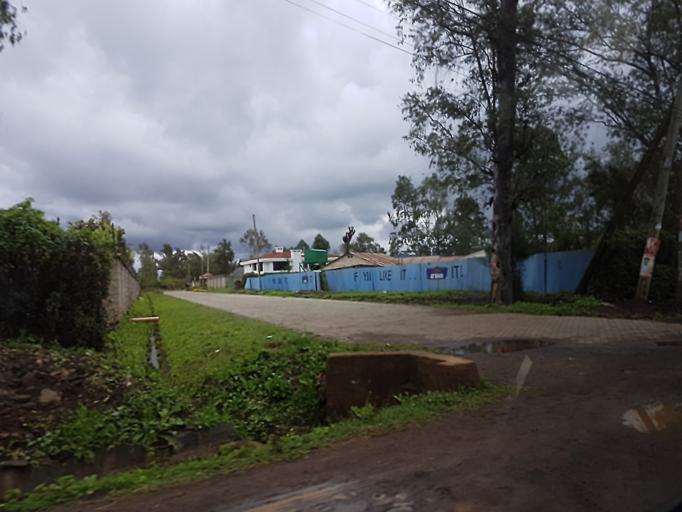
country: KE
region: Kajiado
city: Ngong
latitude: -1.3554
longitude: 36.7348
